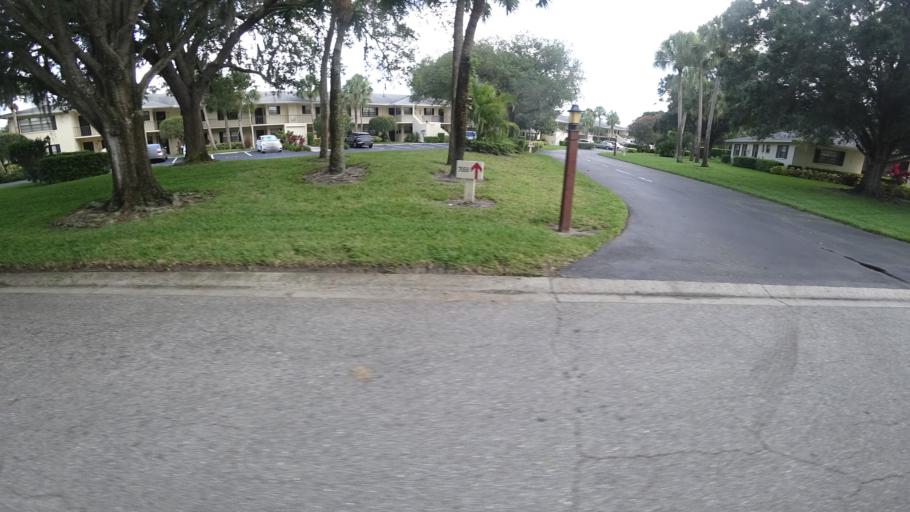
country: US
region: Florida
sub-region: Sarasota County
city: Desoto Lakes
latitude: 27.4155
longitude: -82.4934
